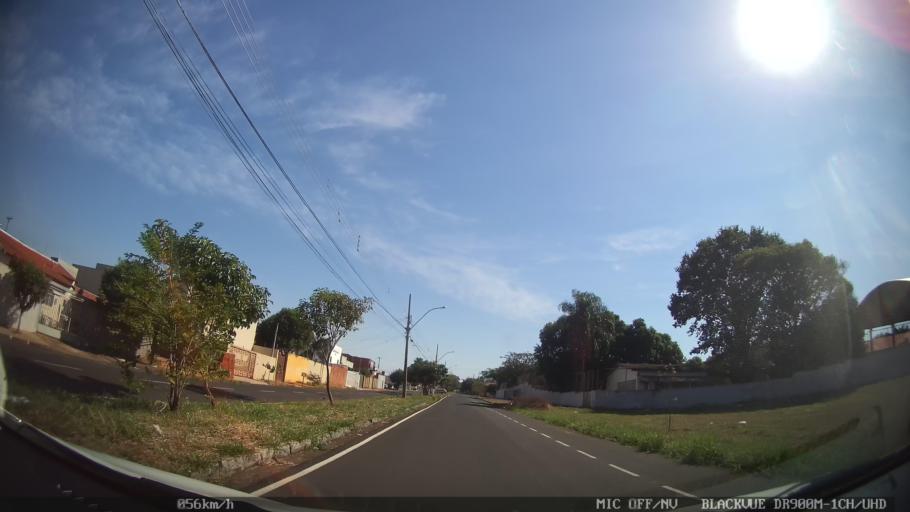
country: BR
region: Sao Paulo
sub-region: Sao Jose Do Rio Preto
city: Sao Jose do Rio Preto
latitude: -20.7810
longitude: -49.4185
